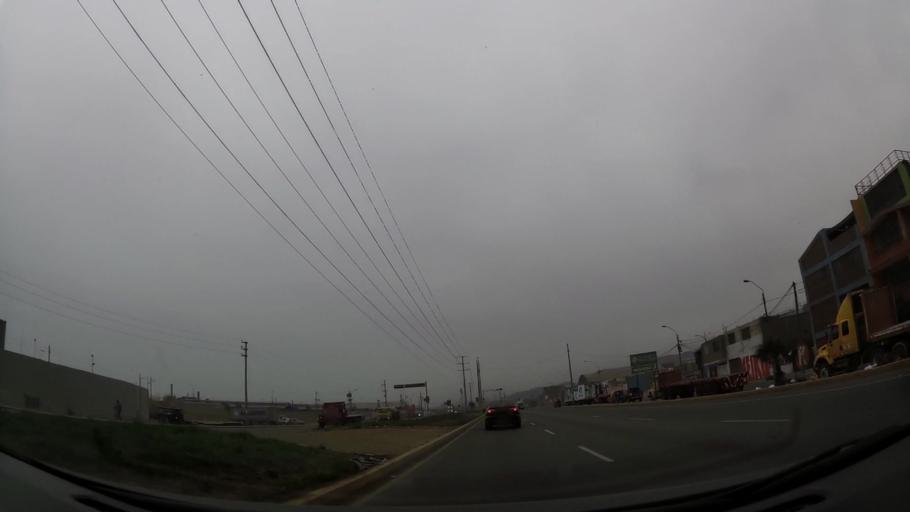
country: PE
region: Lima
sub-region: Lima
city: Independencia
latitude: -11.9703
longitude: -77.1253
